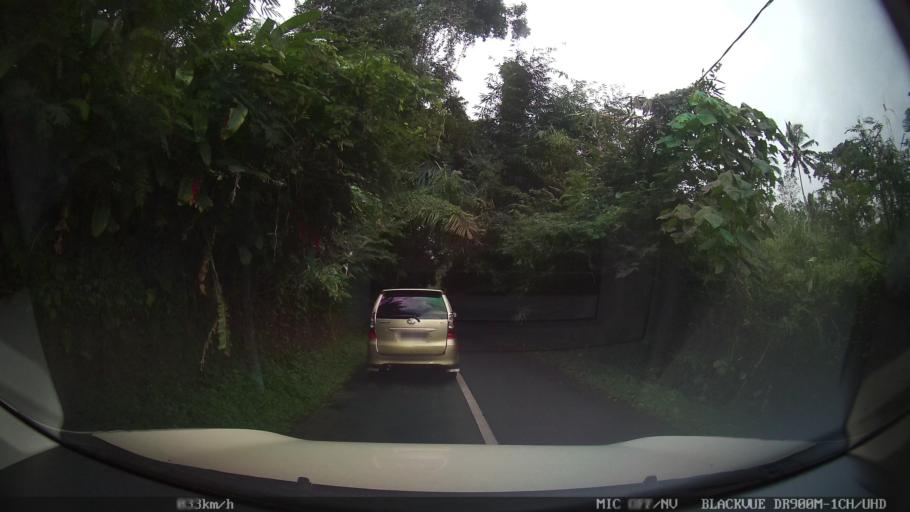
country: ID
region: Bali
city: Peneng
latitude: -8.3623
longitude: 115.1818
